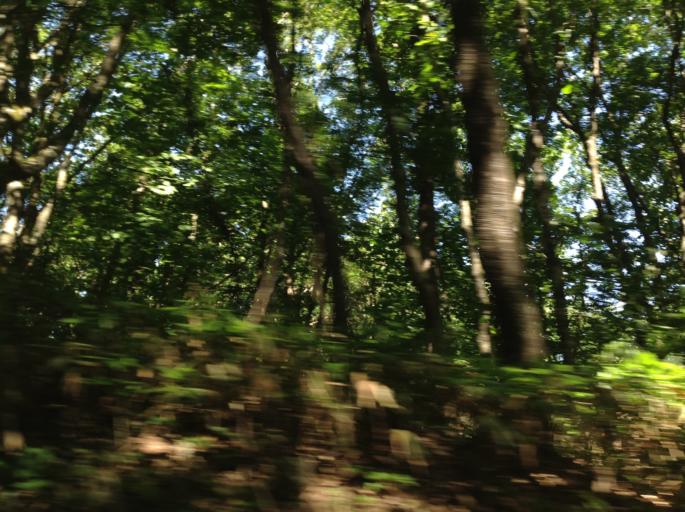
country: JP
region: Akita
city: Kakunodatemachi
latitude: 39.6990
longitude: 140.6694
